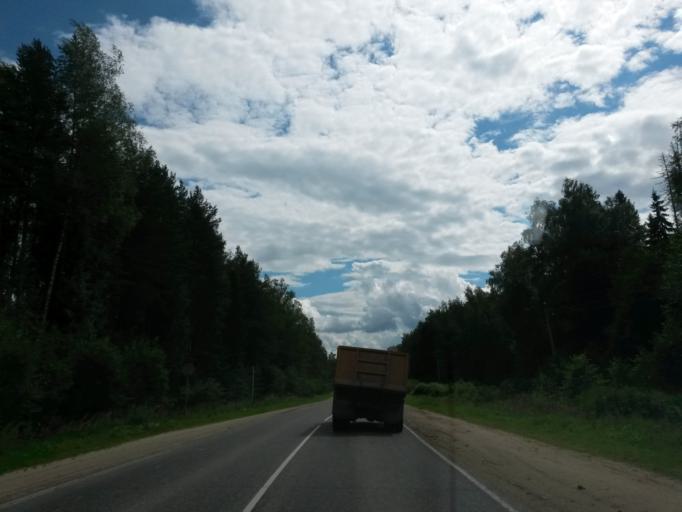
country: RU
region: Ivanovo
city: Novo-Talitsy
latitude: 57.0524
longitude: 40.7348
